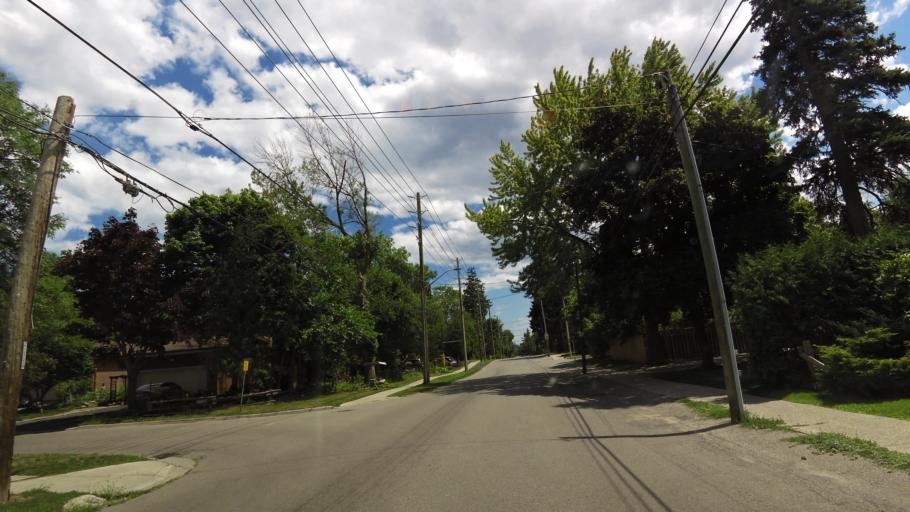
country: CA
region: Ontario
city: Mississauga
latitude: 43.5158
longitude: -79.6224
